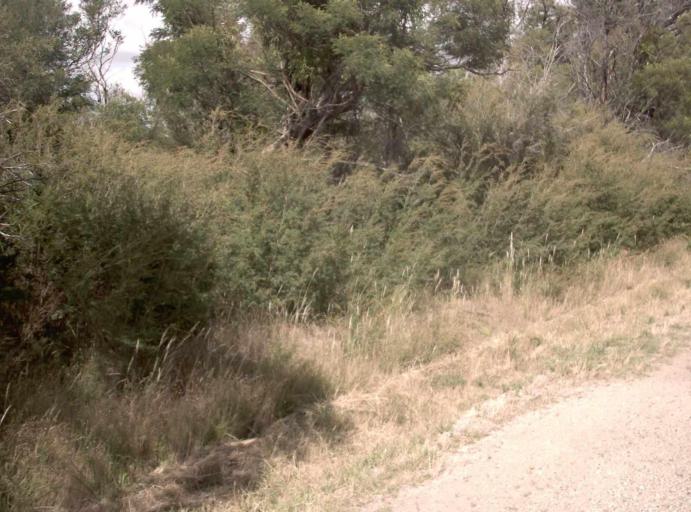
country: AU
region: Victoria
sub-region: Wellington
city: Sale
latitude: -38.1688
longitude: 146.9612
